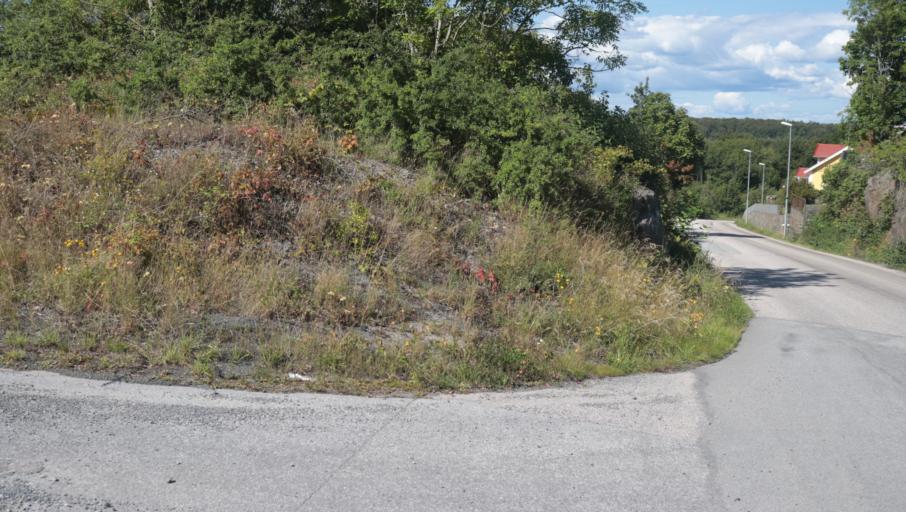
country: SE
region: Blekinge
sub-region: Karlshamns Kommun
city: Karlshamn
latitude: 56.1531
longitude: 14.8523
